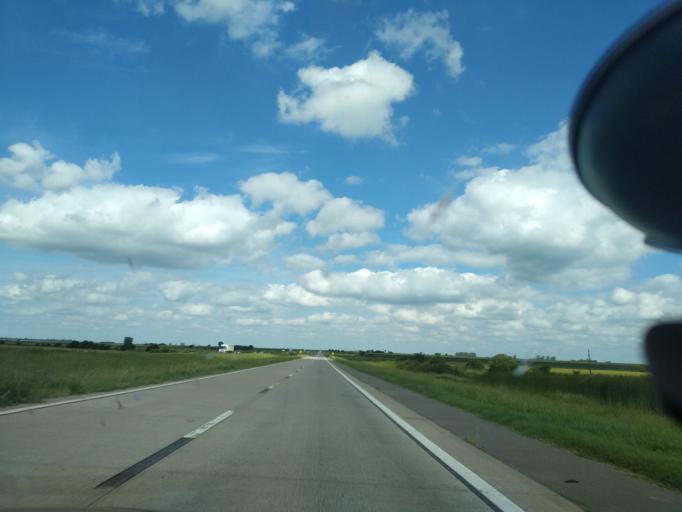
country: AR
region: Santa Fe
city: Canada de Gomez
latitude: -32.8291
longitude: -61.4935
